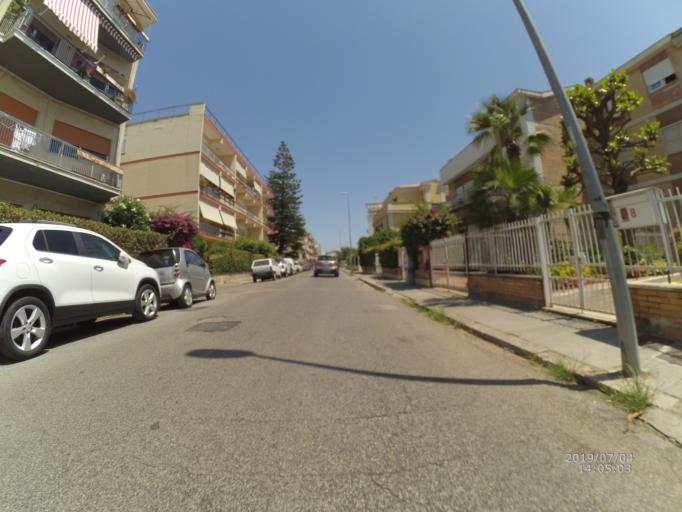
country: IT
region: Latium
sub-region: Provincia di Latina
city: Terracina
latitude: 41.2852
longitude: 13.2490
